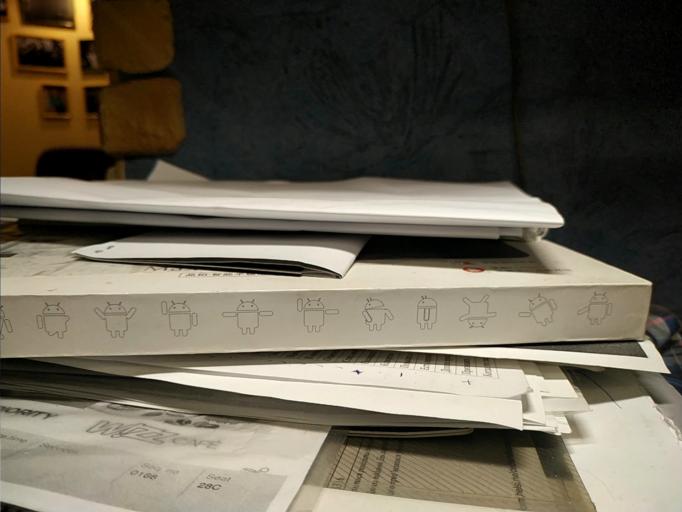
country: RU
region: Tverskaya
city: Zubtsov
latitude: 56.0795
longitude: 34.8066
